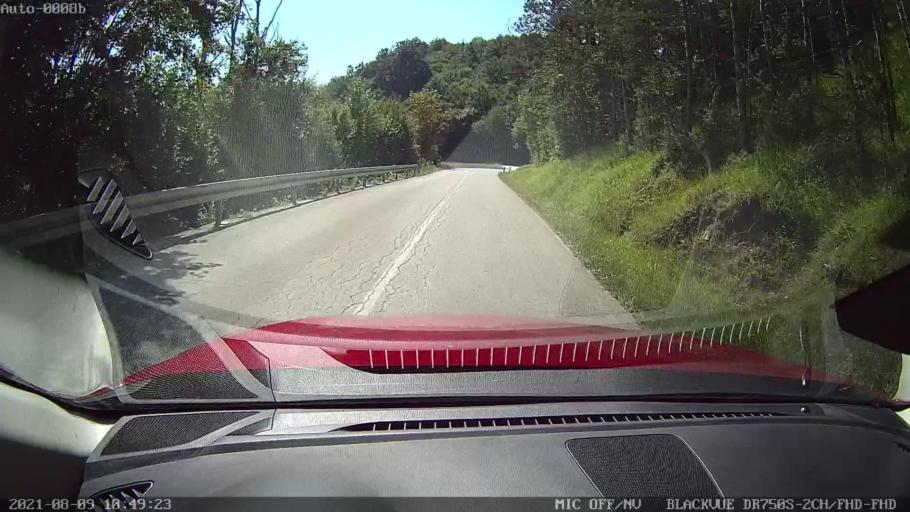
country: HR
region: Istarska
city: Pazin
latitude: 45.2675
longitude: 14.0313
